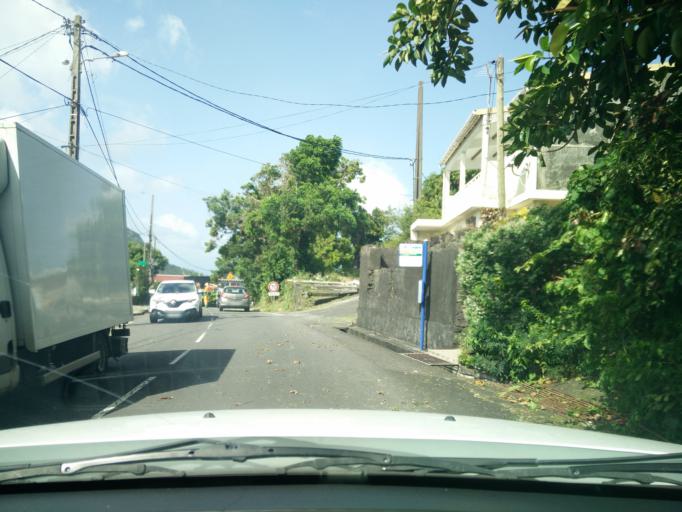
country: GP
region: Guadeloupe
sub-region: Guadeloupe
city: Gourbeyre
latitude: 15.9986
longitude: -61.7007
